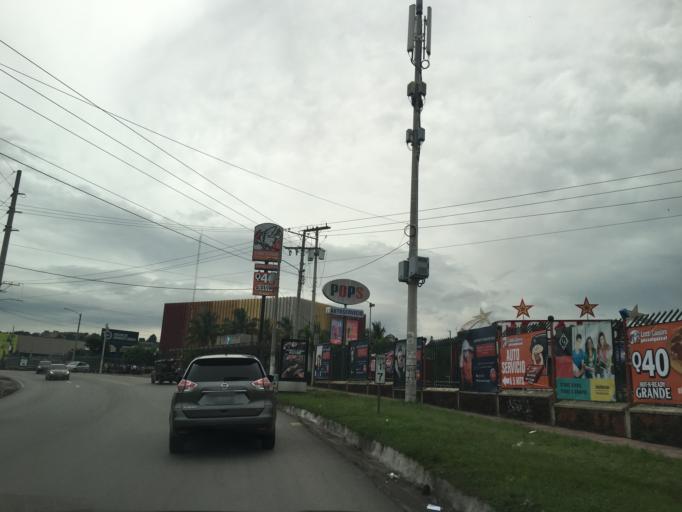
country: GT
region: Guatemala
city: Petapa
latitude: 14.5233
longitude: -90.5631
